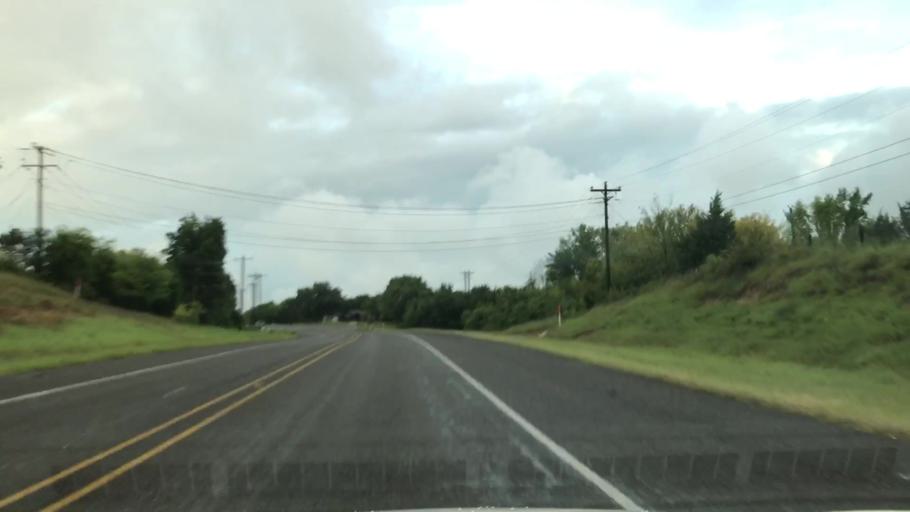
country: US
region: Texas
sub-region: Rockwall County
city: Rockwall
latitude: 32.9751
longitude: -96.4669
